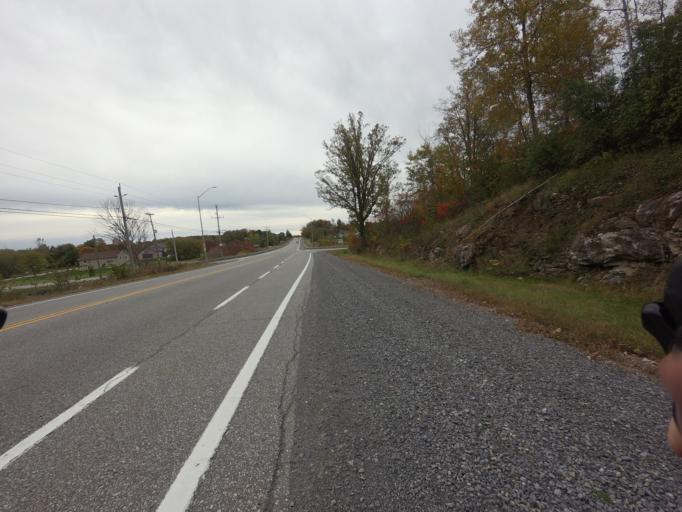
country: CA
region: Ontario
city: Gananoque
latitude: 44.4125
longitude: -76.3075
